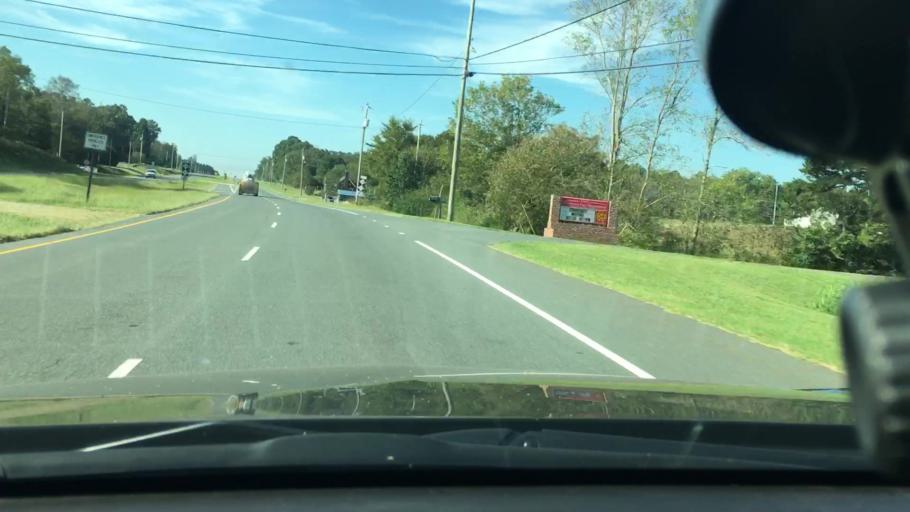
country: US
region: North Carolina
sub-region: Stanly County
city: Albemarle
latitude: 35.3040
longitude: -80.2774
